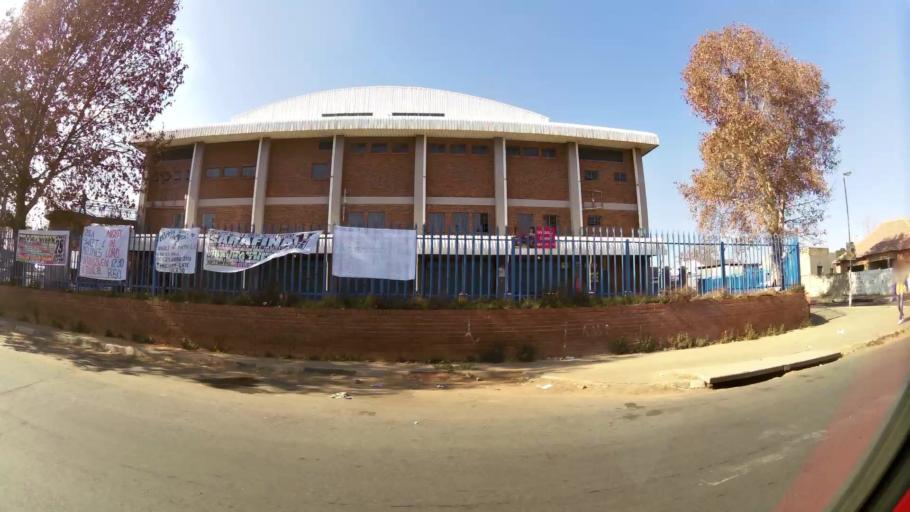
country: ZA
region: Gauteng
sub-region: City of Johannesburg Metropolitan Municipality
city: Soweto
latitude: -26.2350
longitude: 27.9227
